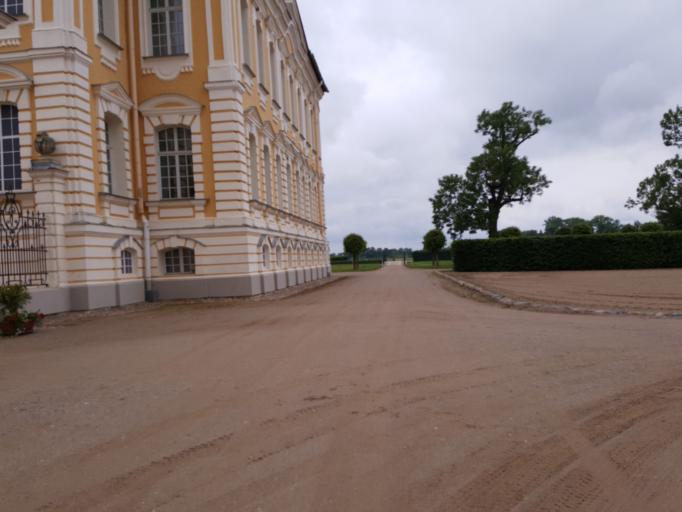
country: LV
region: Rundales
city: Pilsrundale
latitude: 56.4140
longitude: 24.0258
